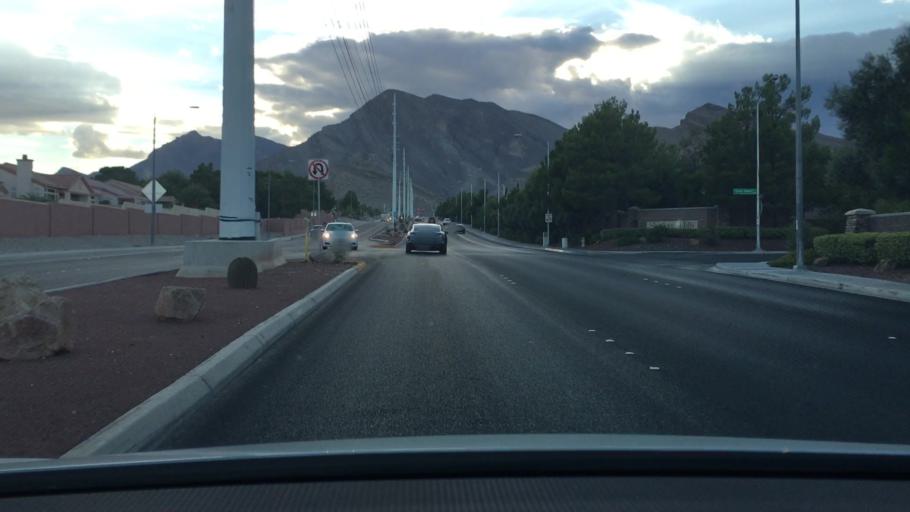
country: US
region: Nevada
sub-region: Clark County
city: Summerlin South
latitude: 36.2183
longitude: -115.3176
